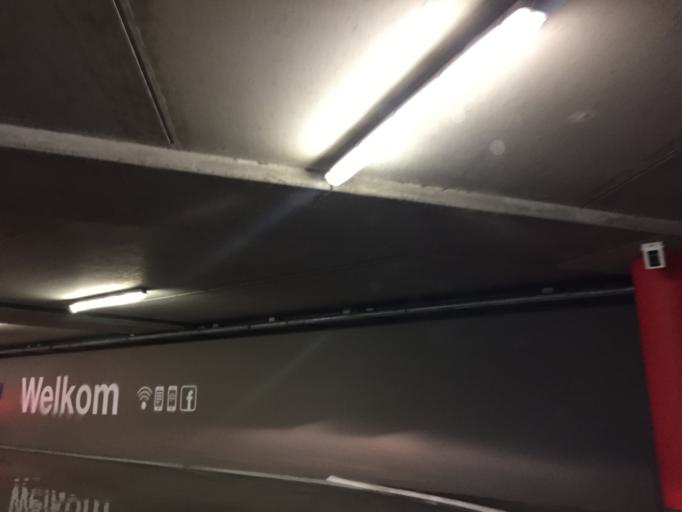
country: NL
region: South Holland
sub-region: Gemeente Zoetermeer
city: Zoetermeer
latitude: 52.0612
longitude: 4.4838
